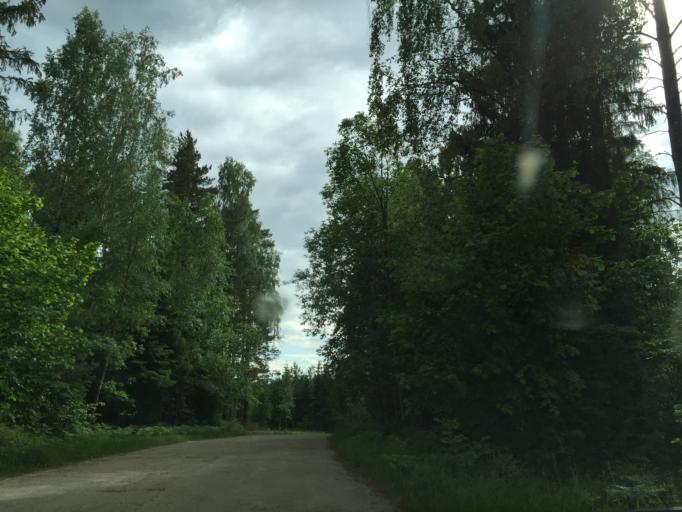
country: LV
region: Dobeles Rajons
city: Dobele
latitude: 56.6492
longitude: 23.1928
